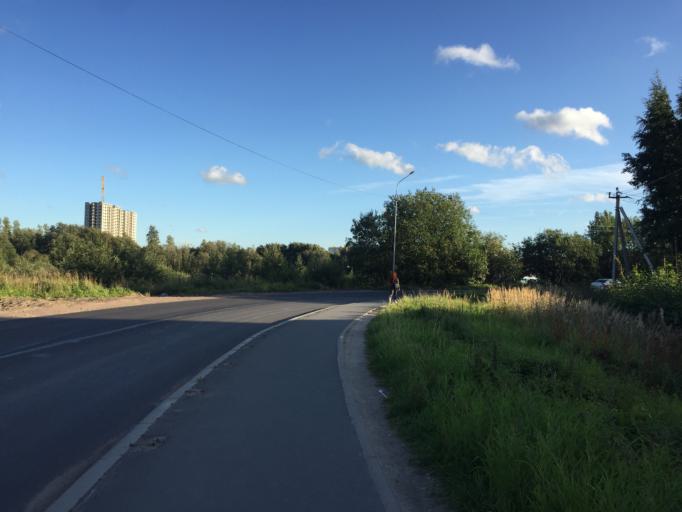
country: RU
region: Leningrad
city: Murino
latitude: 60.0569
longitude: 30.4597
